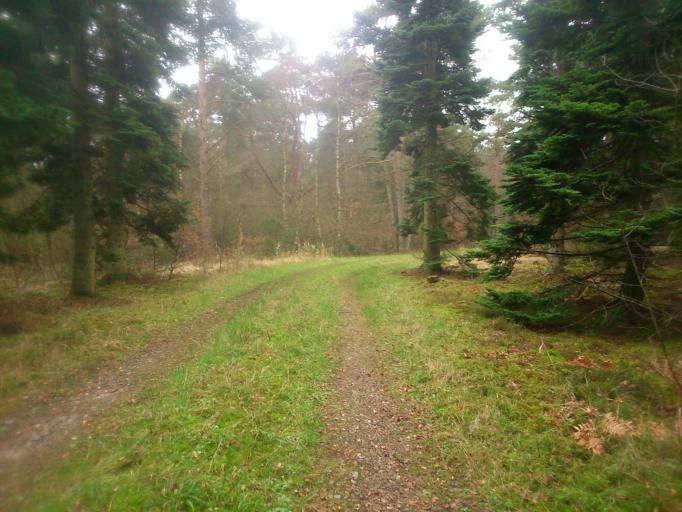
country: DK
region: Central Jutland
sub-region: Viborg Kommune
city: Bjerringbro
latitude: 56.3917
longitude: 9.7149
